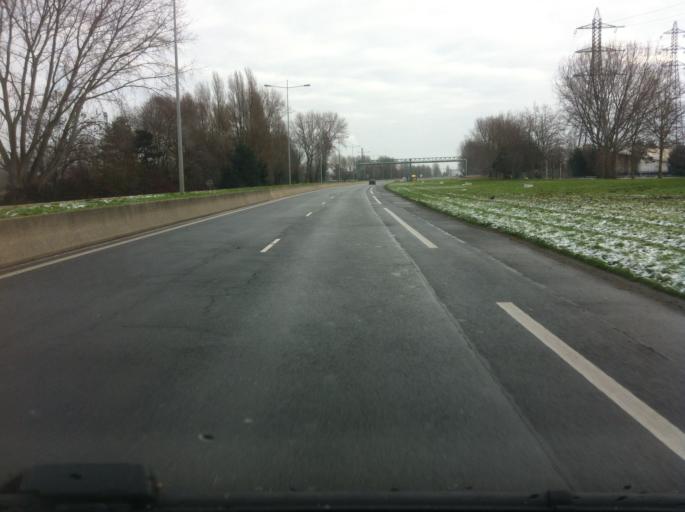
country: FR
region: Haute-Normandie
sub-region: Departement de la Seine-Maritime
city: Harfleur
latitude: 49.4876
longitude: 0.2099
